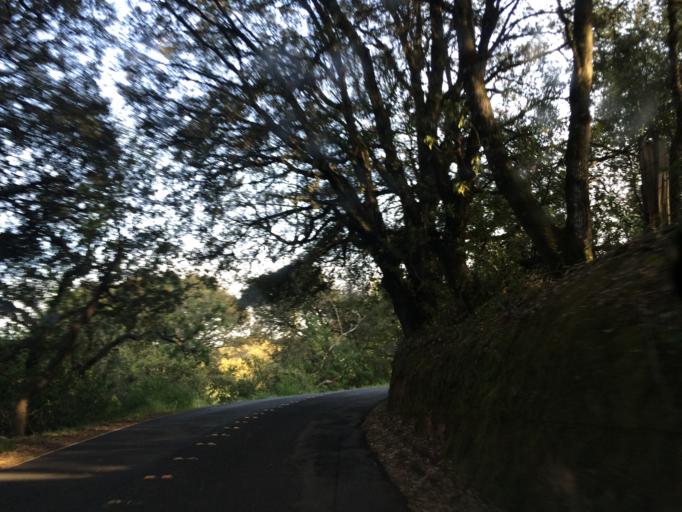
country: US
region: California
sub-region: Santa Clara County
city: Los Altos Hills
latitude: 37.3328
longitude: -122.1737
